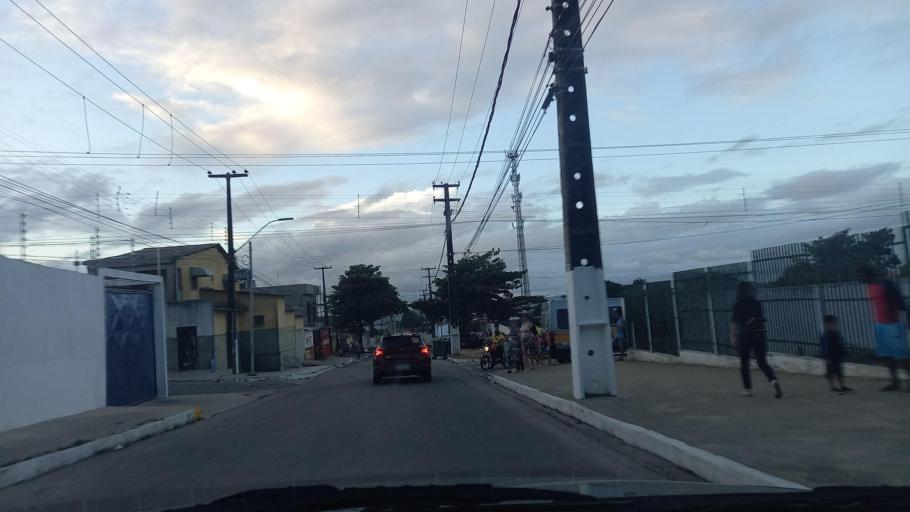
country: BR
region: Pernambuco
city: Garanhuns
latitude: -8.8777
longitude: -36.4656
